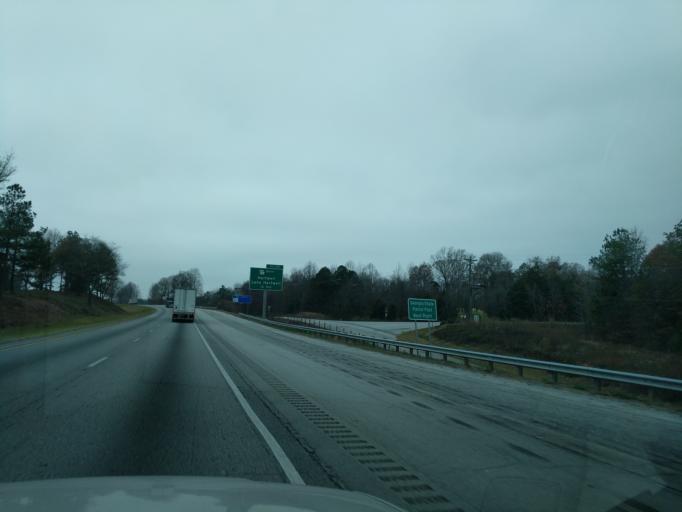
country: US
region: Georgia
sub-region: Franklin County
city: Gumlog
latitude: 34.4778
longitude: -83.0444
